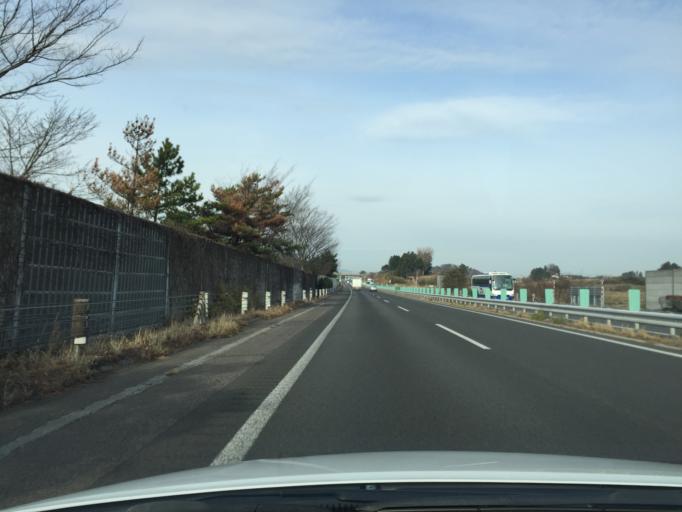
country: JP
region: Fukushima
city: Motomiya
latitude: 37.5014
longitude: 140.3809
